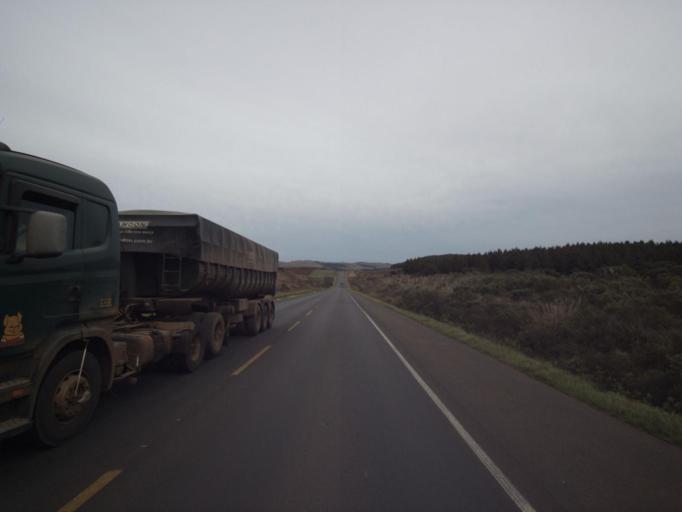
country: BR
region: Parana
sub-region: Palmas
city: Palmas
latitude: -26.6686
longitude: -51.5490
